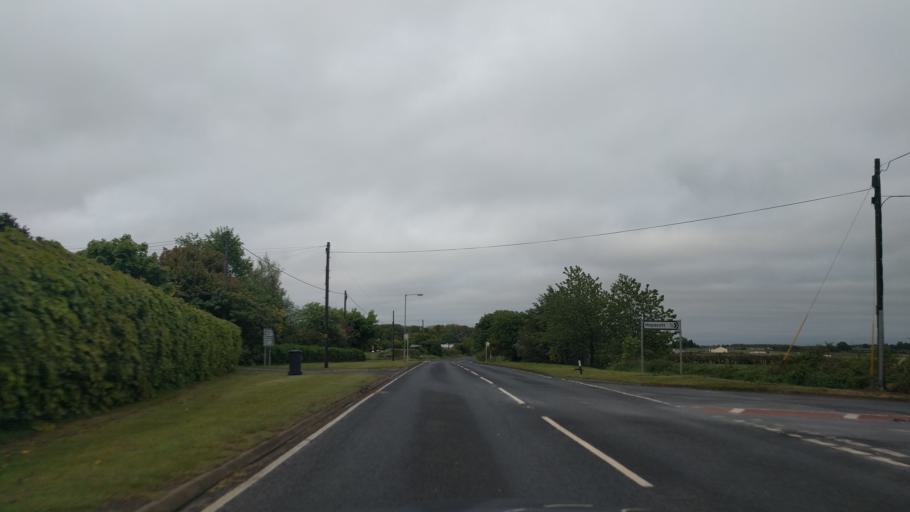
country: GB
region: England
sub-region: Northumberland
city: Pegswood
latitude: 55.1628
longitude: -1.6445
